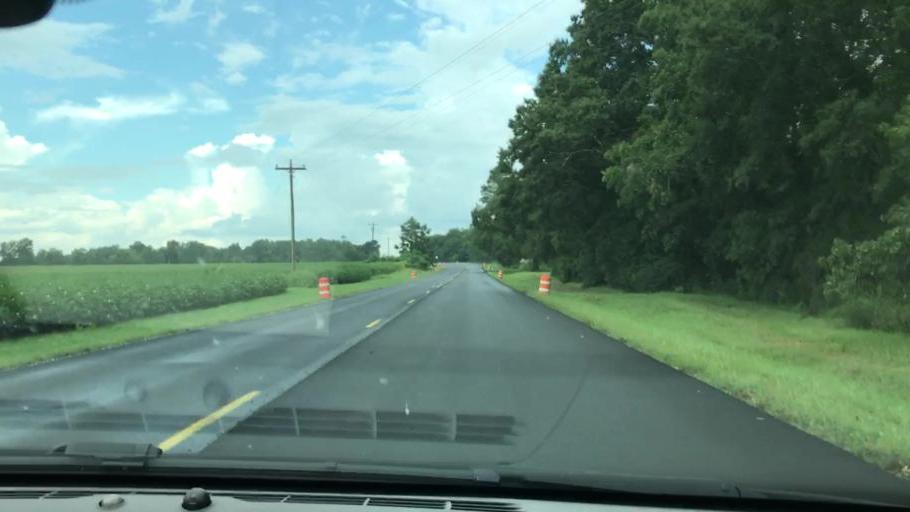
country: US
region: Georgia
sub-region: Early County
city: Blakely
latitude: 31.4317
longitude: -84.9717
